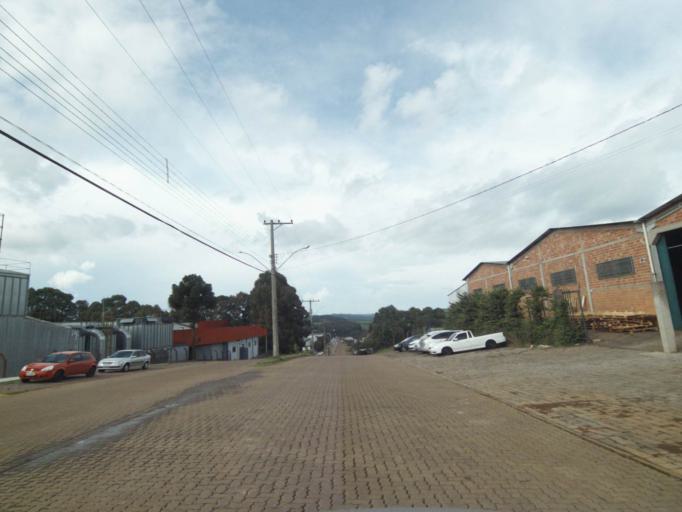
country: BR
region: Rio Grande do Sul
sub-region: Lagoa Vermelha
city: Lagoa Vermelha
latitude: -28.2256
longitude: -51.5116
